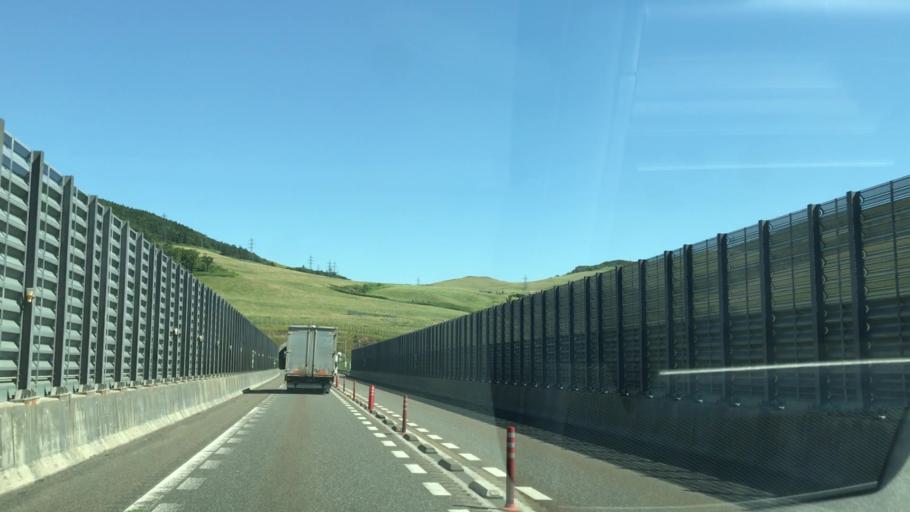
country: JP
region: Hokkaido
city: Shimo-furano
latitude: 43.0605
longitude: 142.7159
